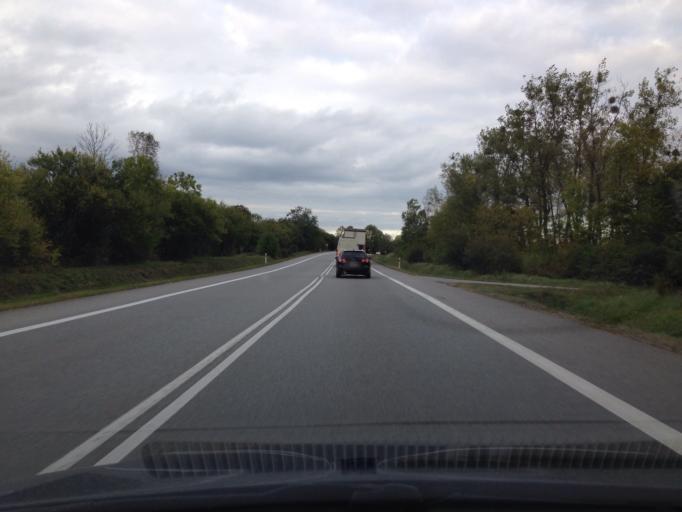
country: PL
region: Kujawsko-Pomorskie
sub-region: Powiat lipnowski
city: Skepe
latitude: 52.8563
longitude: 19.2716
